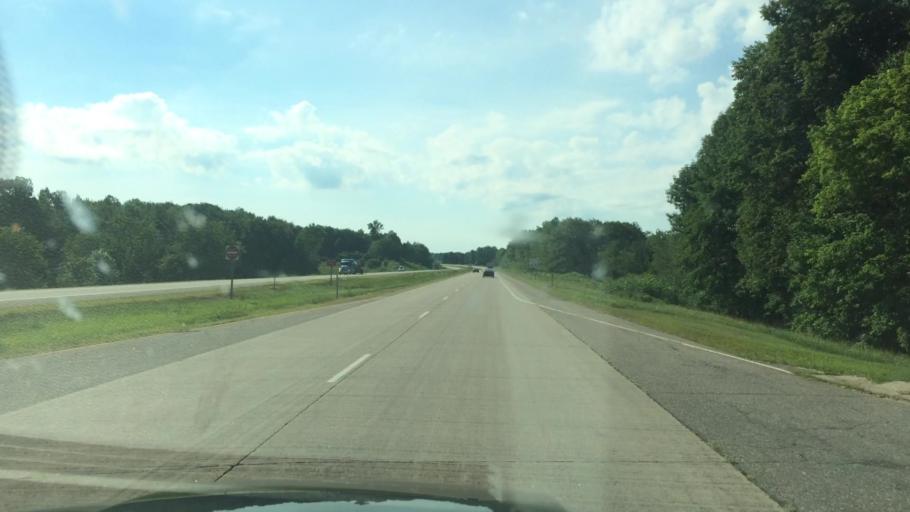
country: US
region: Wisconsin
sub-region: Shawano County
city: Wittenberg
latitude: 44.8103
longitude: -89.0412
